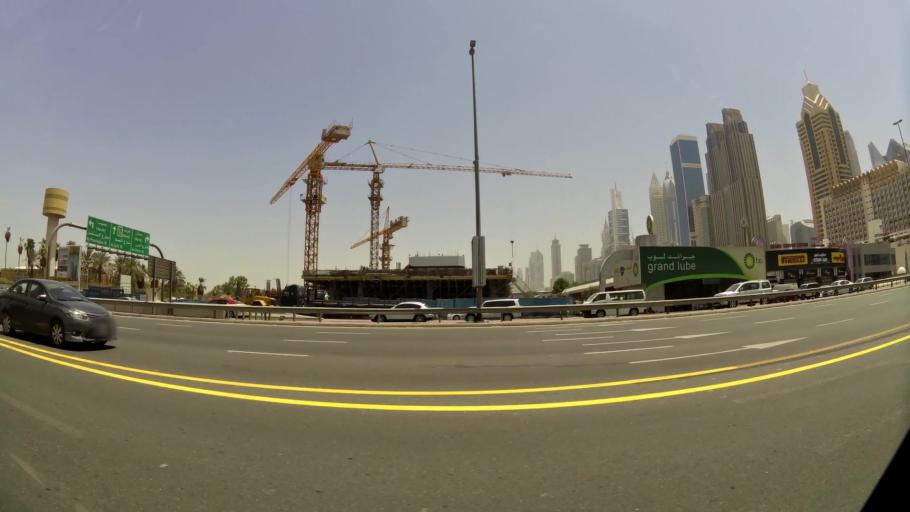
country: AE
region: Dubai
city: Dubai
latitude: 25.2063
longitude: 55.2673
